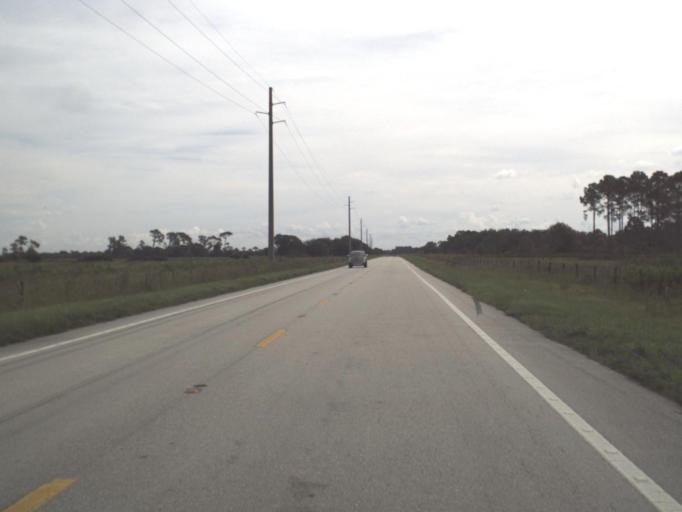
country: US
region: Florida
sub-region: Highlands County
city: Placid Lakes
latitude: 27.2088
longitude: -81.4908
